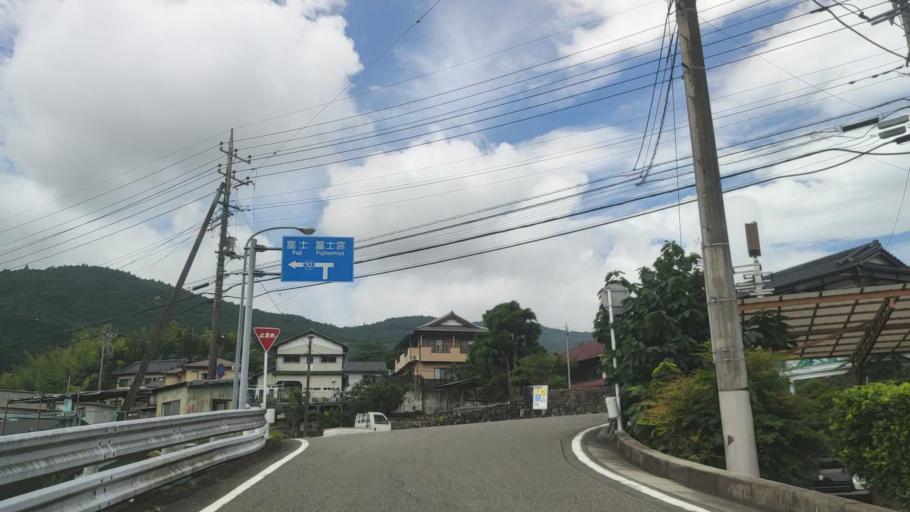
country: JP
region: Shizuoka
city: Fujinomiya
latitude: 35.2224
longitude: 138.5152
